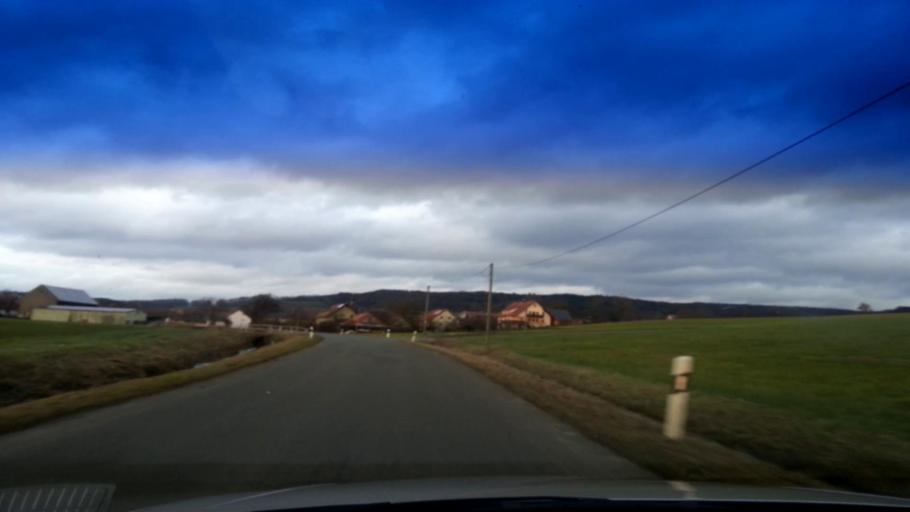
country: DE
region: Bavaria
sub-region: Upper Franconia
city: Schesslitz
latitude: 50.0006
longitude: 11.0157
